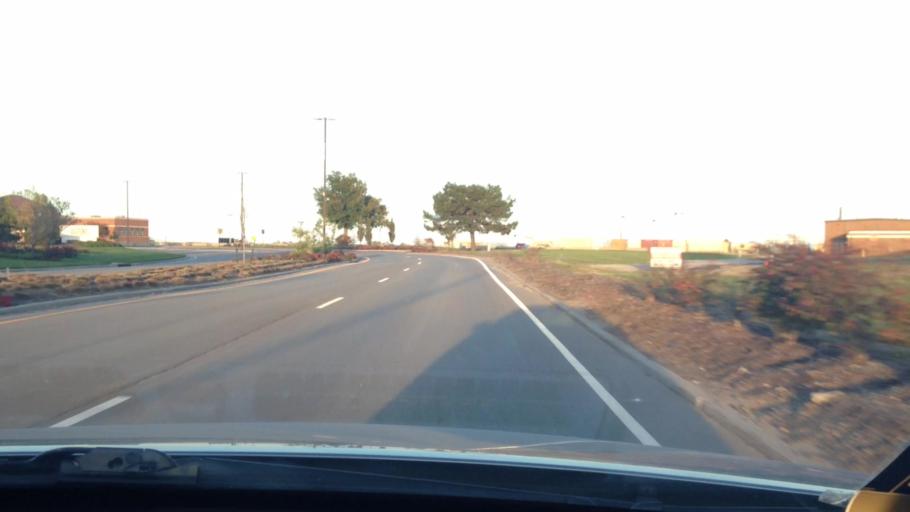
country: US
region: Kansas
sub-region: Johnson County
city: Gardner
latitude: 38.8369
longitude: -94.8976
